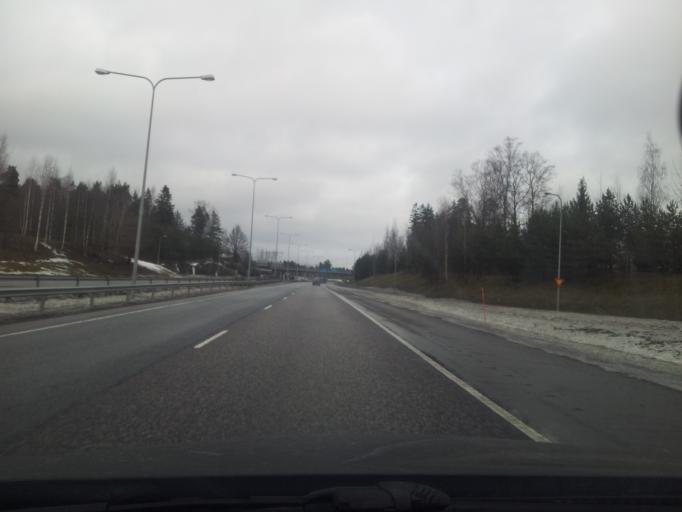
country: FI
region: Uusimaa
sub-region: Helsinki
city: Espoo
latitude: 60.2118
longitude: 24.6320
